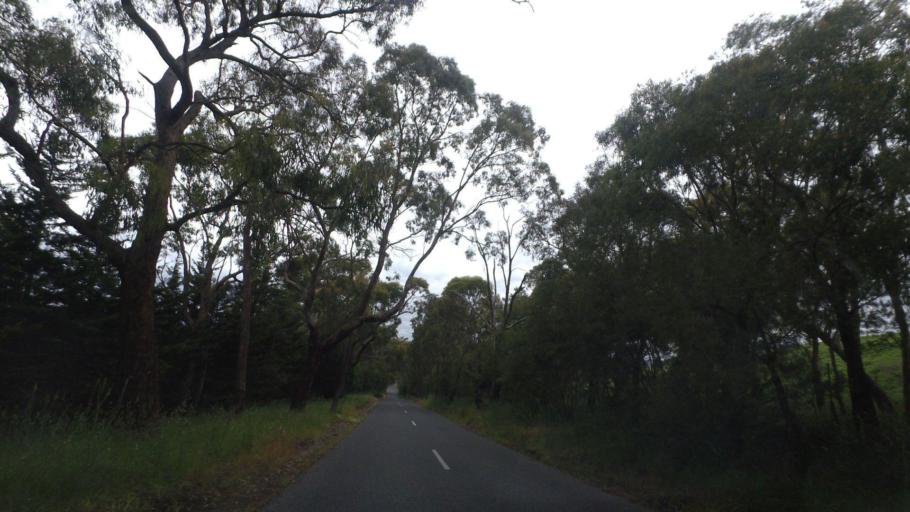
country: AU
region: Victoria
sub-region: Yarra Ranges
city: Mount Evelyn
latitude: -37.7375
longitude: 145.3987
